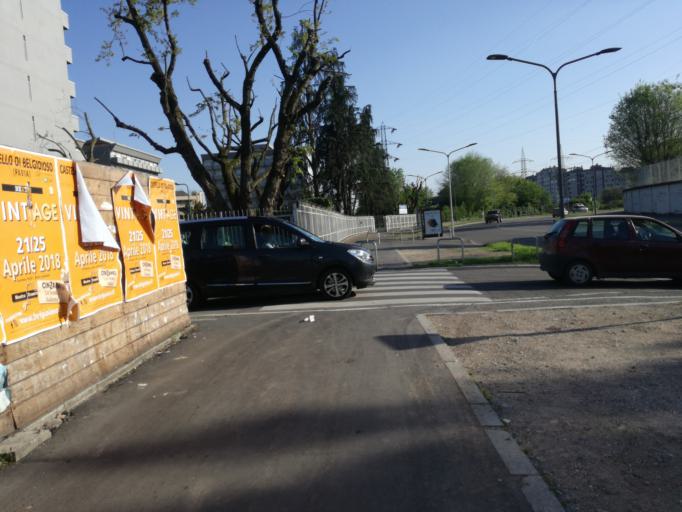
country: IT
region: Lombardy
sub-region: Citta metropolitana di Milano
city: Milano
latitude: 45.4361
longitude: 9.1879
